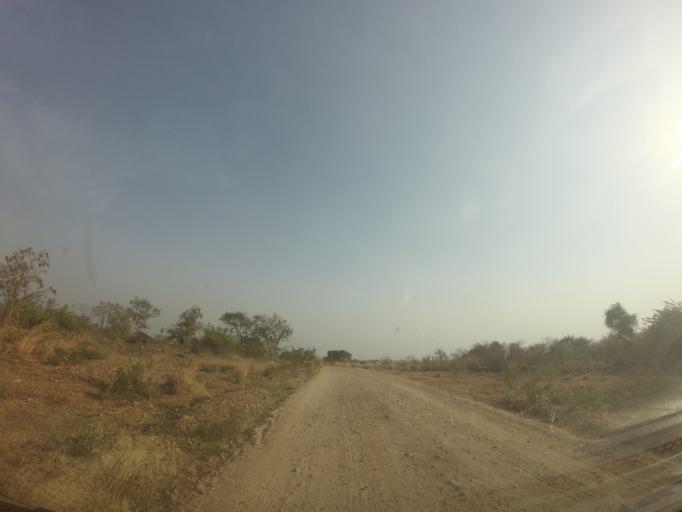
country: UG
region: Northern Region
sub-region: Maracha District
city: Maracha
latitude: 3.1135
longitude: 31.1569
